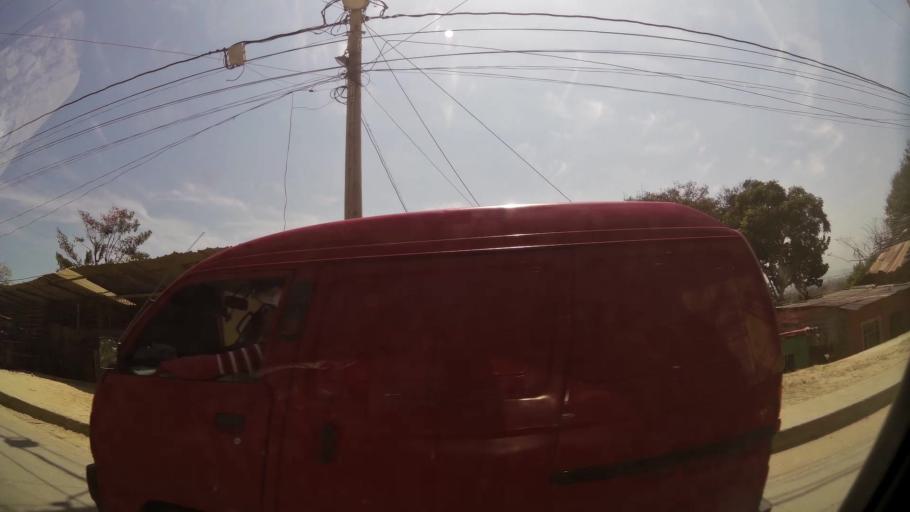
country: CO
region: Atlantico
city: Barranquilla
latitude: 10.9638
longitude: -74.8119
